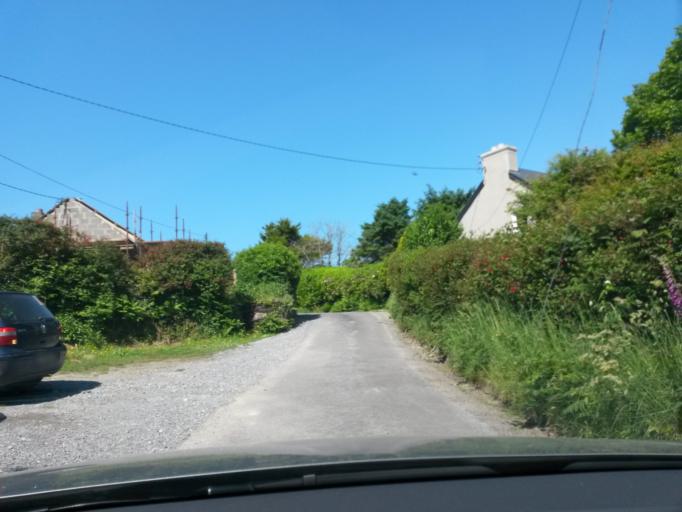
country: IE
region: Munster
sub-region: Ciarrai
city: Cahersiveen
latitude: 51.7332
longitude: -9.9602
